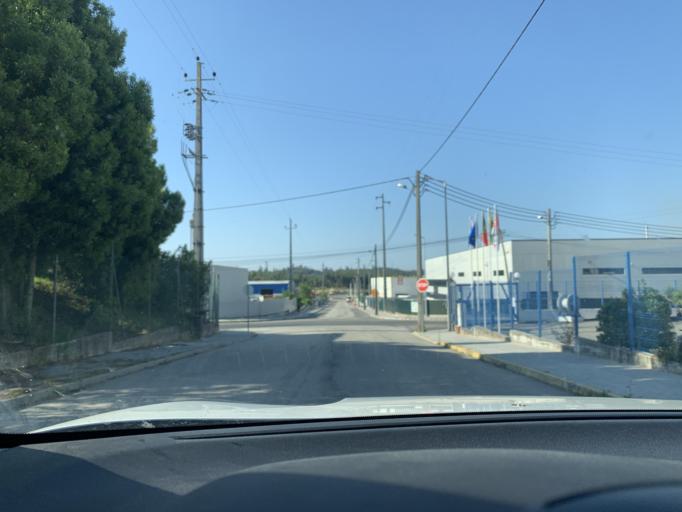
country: PT
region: Viseu
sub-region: Concelho de Tondela
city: Tondela
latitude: 40.4847
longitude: -8.0939
